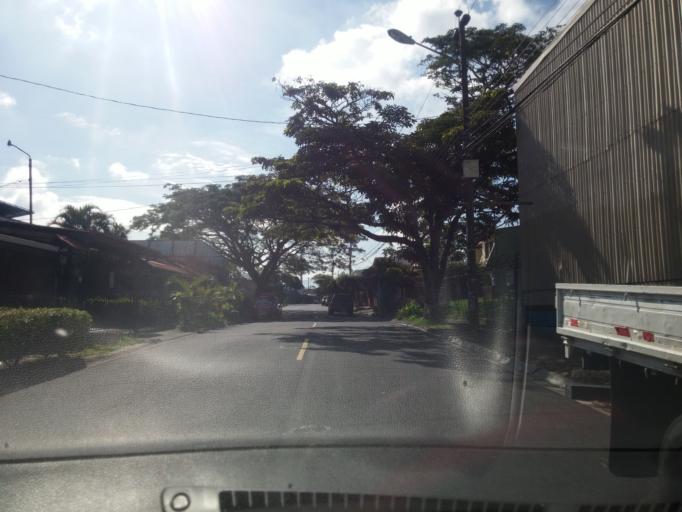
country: CR
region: Heredia
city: San Francisco
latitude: 9.9976
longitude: -84.1303
